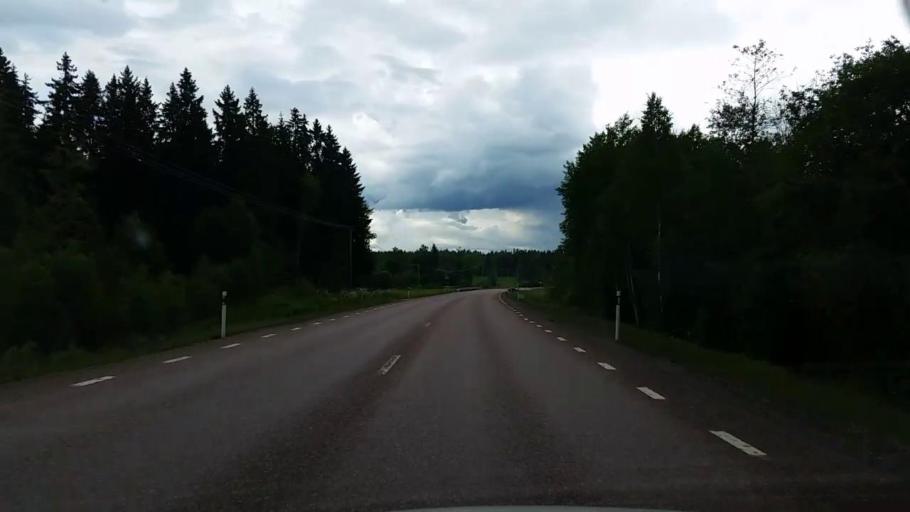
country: SE
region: Gaevleborg
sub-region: Hofors Kommun
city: Hofors
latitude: 60.5124
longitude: 16.4347
